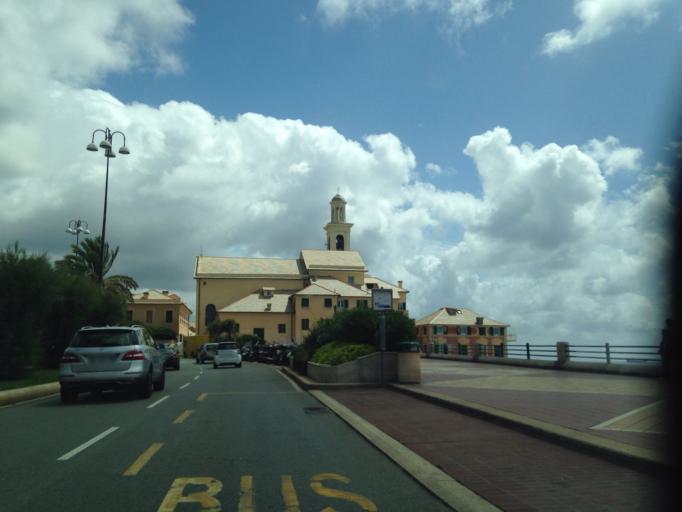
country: IT
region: Liguria
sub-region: Provincia di Genova
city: San Teodoro
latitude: 44.3900
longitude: 8.9720
